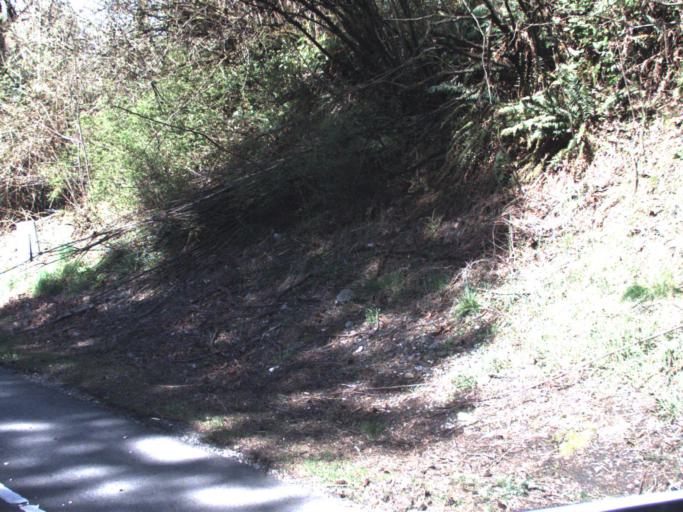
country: US
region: Washington
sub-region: King County
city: Lea Hill
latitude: 47.2841
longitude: -122.1715
